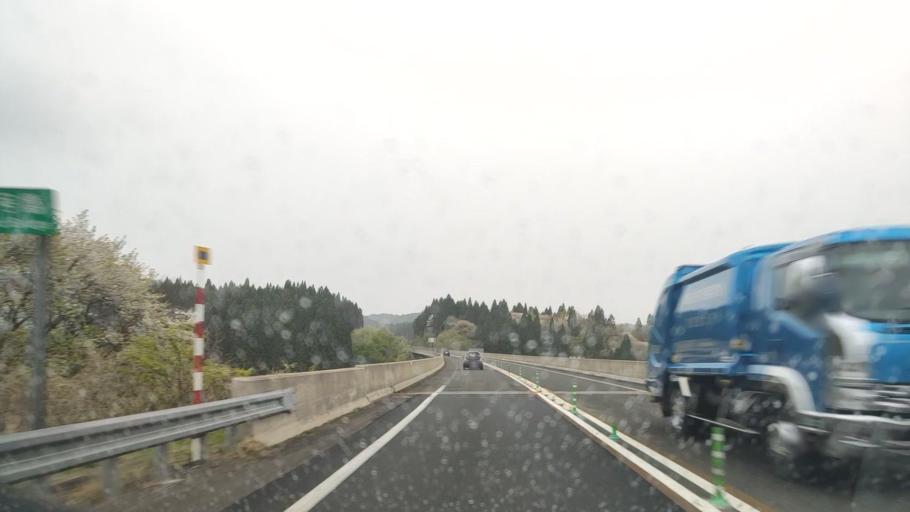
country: JP
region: Akita
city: Noshiromachi
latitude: 40.2089
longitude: 140.1848
